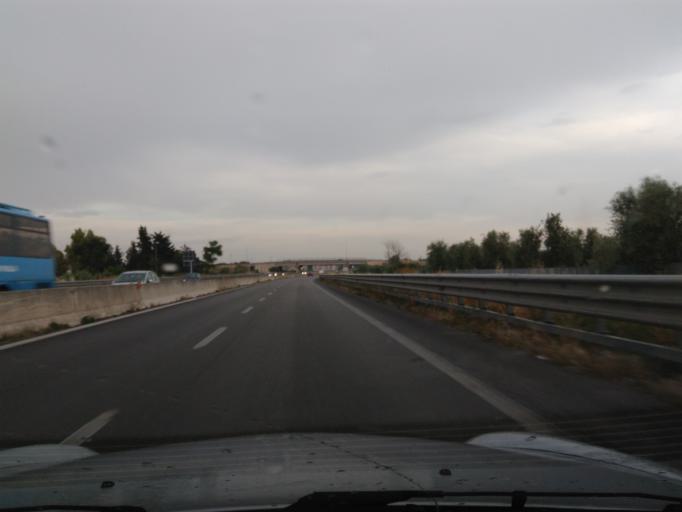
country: IT
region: Apulia
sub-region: Provincia di Bari
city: Molfetta
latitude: 41.1977
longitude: 16.5783
